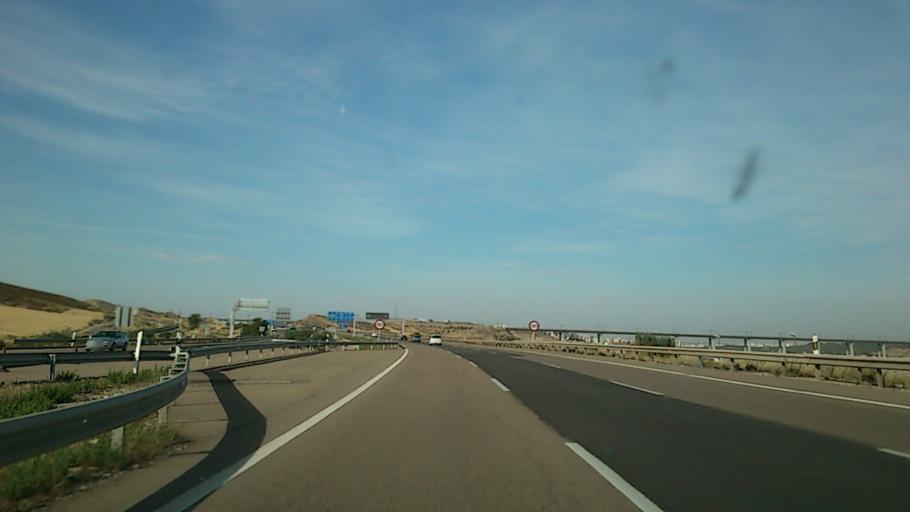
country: ES
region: Aragon
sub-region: Provincia de Zaragoza
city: Cuarte de Huerva
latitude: 41.5991
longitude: -0.9386
